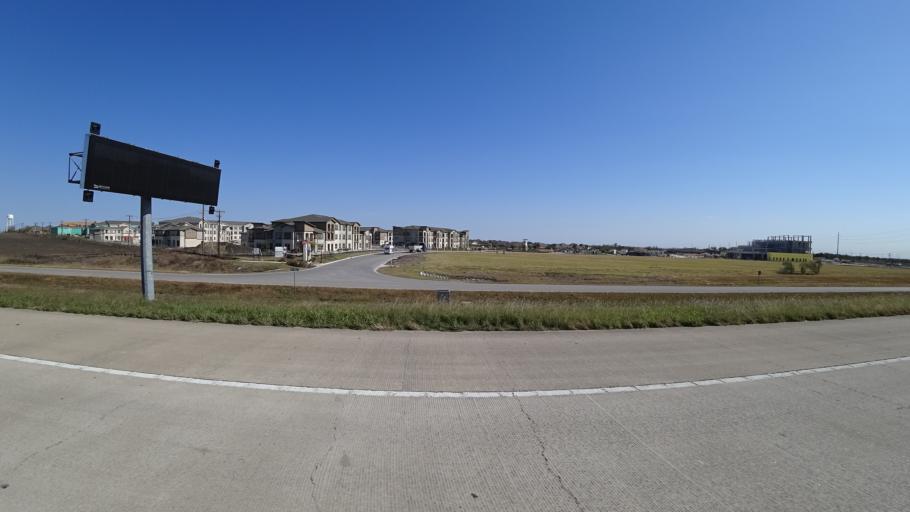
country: US
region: Texas
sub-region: Travis County
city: Pflugerville
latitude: 30.4537
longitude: -97.5940
